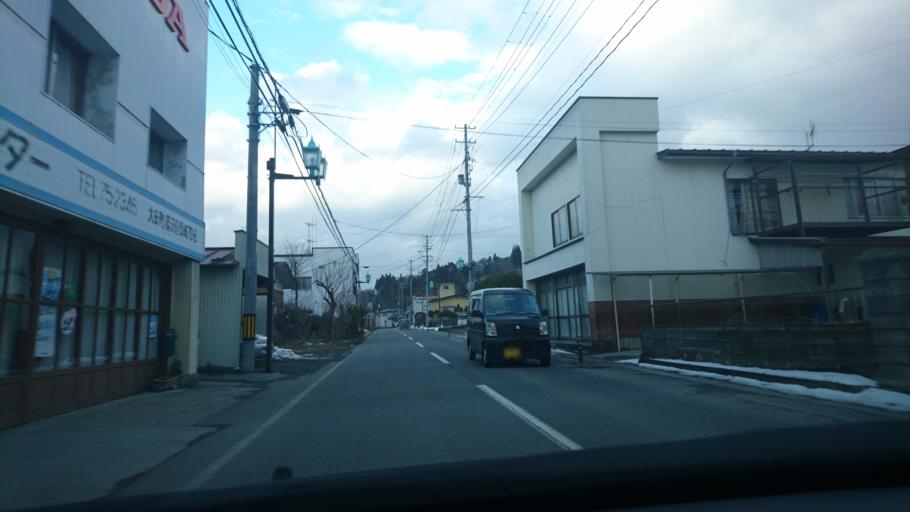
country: JP
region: Iwate
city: Ichinoseki
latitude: 38.9956
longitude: 141.3311
